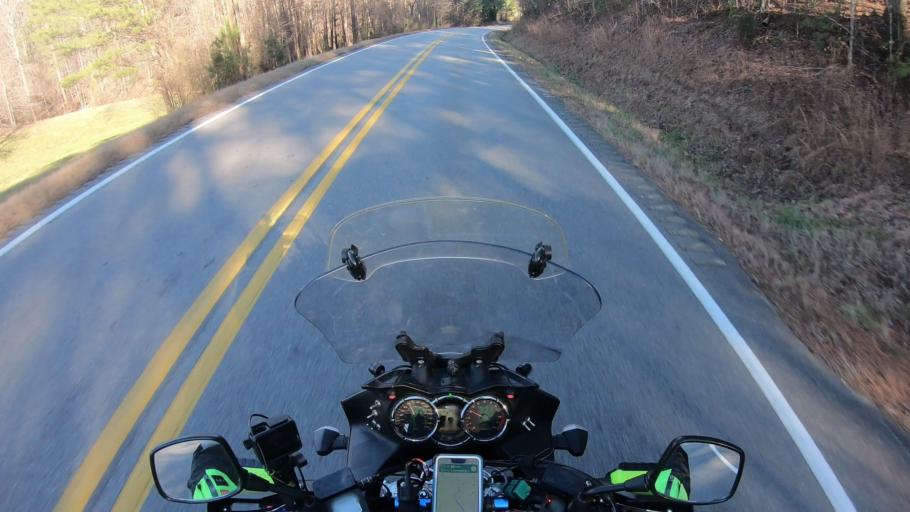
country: US
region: Alabama
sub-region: Cleburne County
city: Heflin
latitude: 33.6688
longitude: -85.5686
